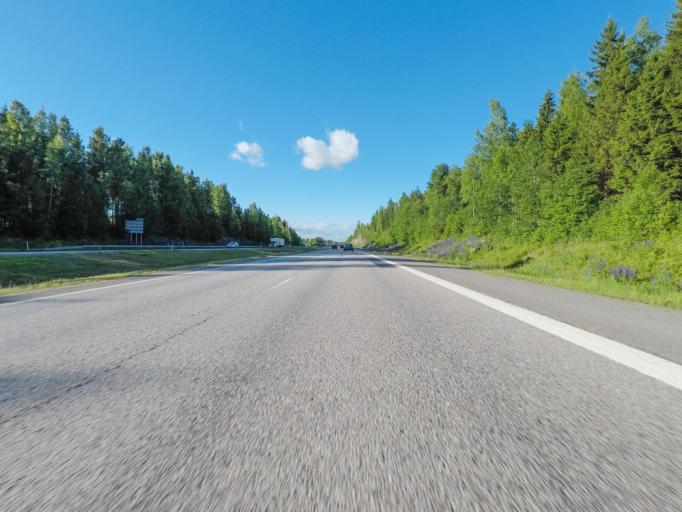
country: FI
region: Uusimaa
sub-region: Helsinki
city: Maentsaelae
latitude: 60.6321
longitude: 25.2928
